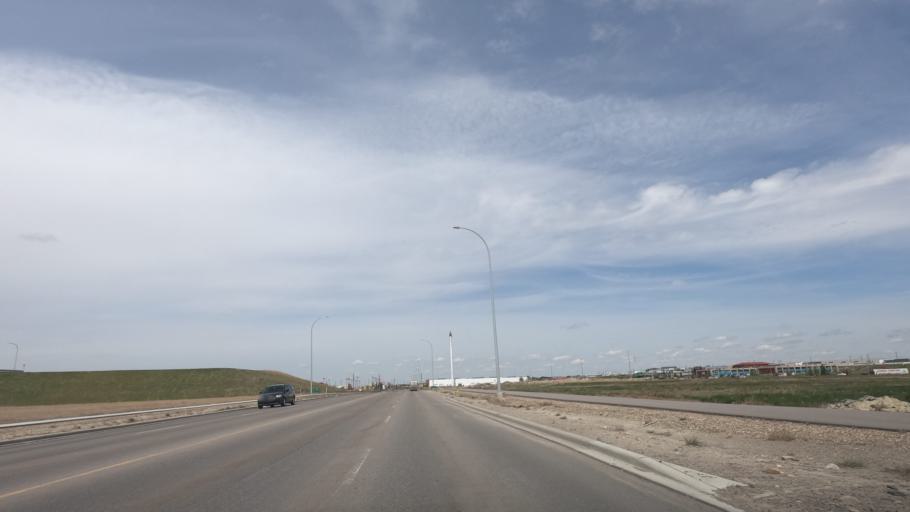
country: CA
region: Alberta
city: Airdrie
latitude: 51.2547
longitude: -114.0050
